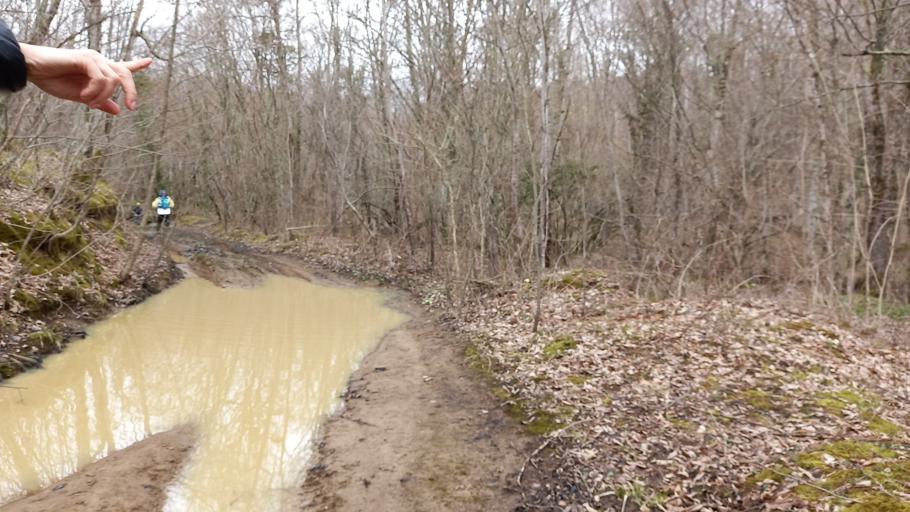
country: RU
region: Krasnodarskiy
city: Pshada
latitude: 44.4904
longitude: 38.3926
